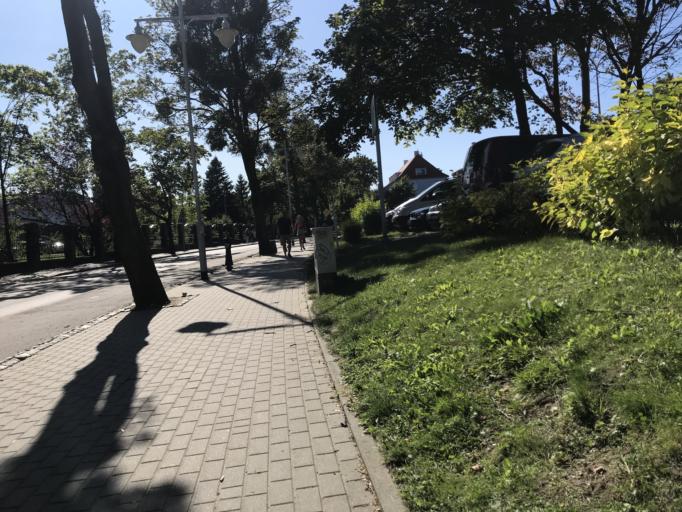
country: PL
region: Pomeranian Voivodeship
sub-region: Sopot
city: Sopot
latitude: 54.4801
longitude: 18.5601
